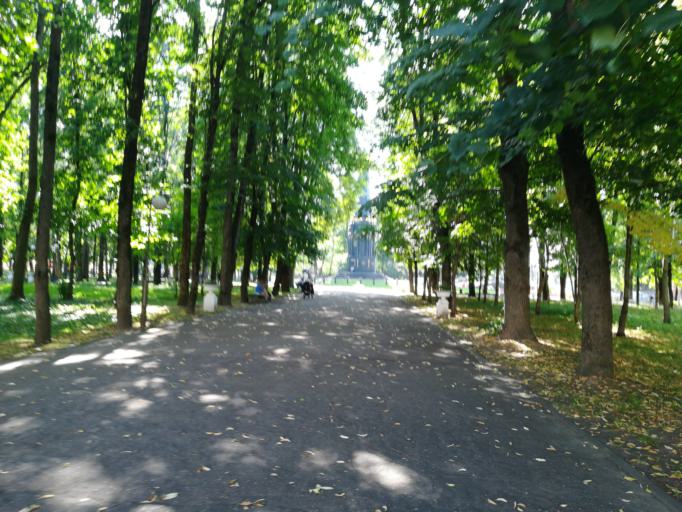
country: RU
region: Smolensk
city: Smolensk
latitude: 54.7839
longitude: 32.0410
